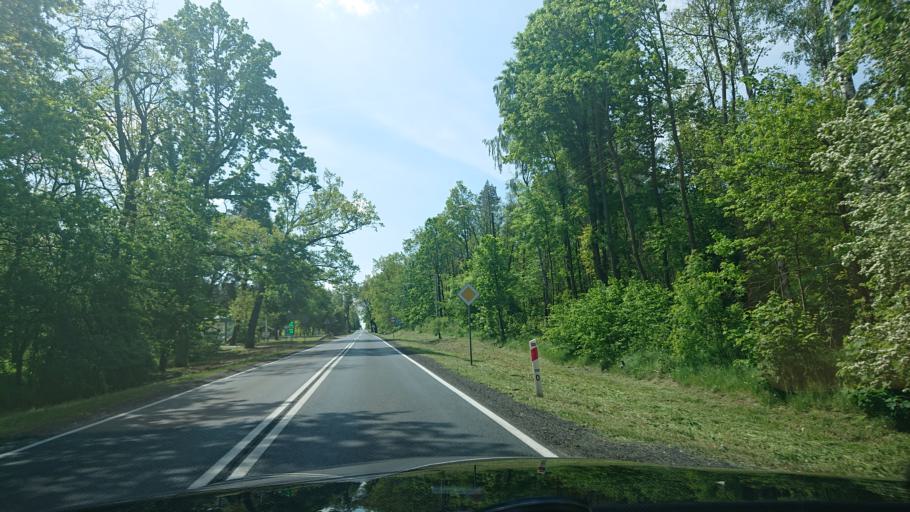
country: PL
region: Greater Poland Voivodeship
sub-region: Powiat gnieznienski
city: Gniezno
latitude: 52.4938
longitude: 17.5940
